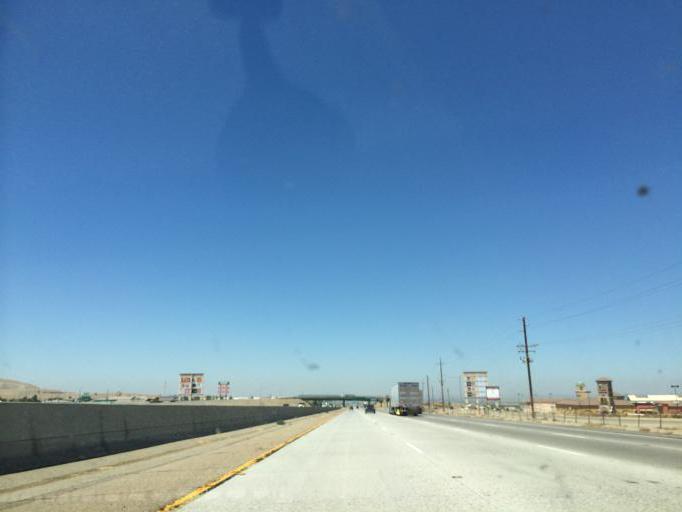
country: US
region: California
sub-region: Kern County
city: Frazier Park
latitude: 34.9813
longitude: -118.9436
